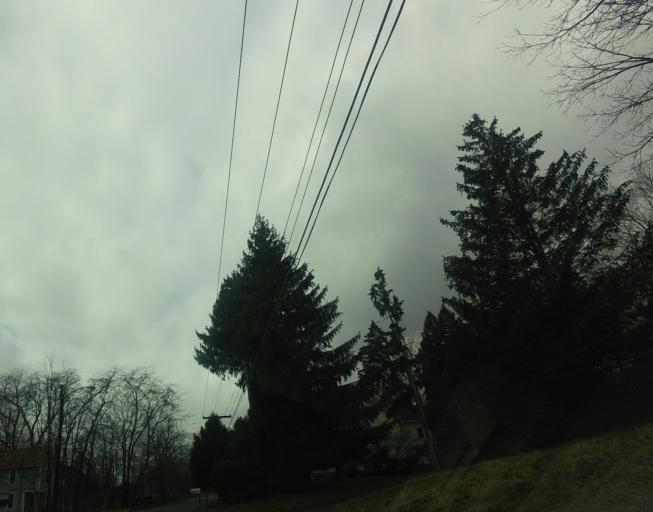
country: US
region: New York
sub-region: Tompkins County
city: Ithaca
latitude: 42.4364
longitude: -76.5231
